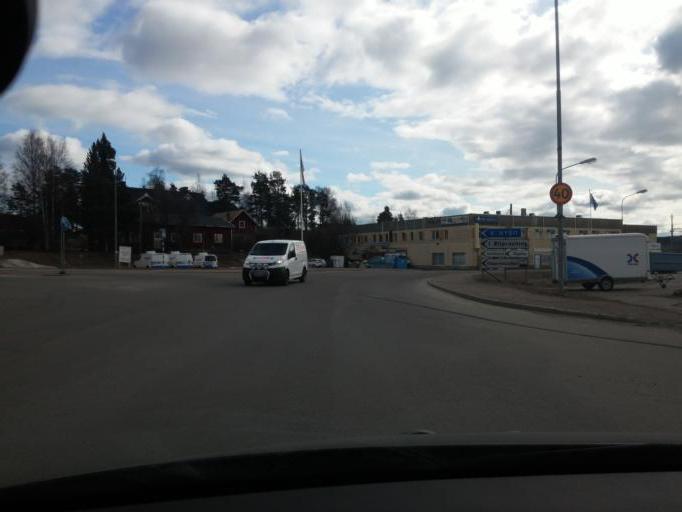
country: SE
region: Gaevleborg
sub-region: Ljusdals Kommun
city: Ljusdal
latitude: 61.8238
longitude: 16.1105
